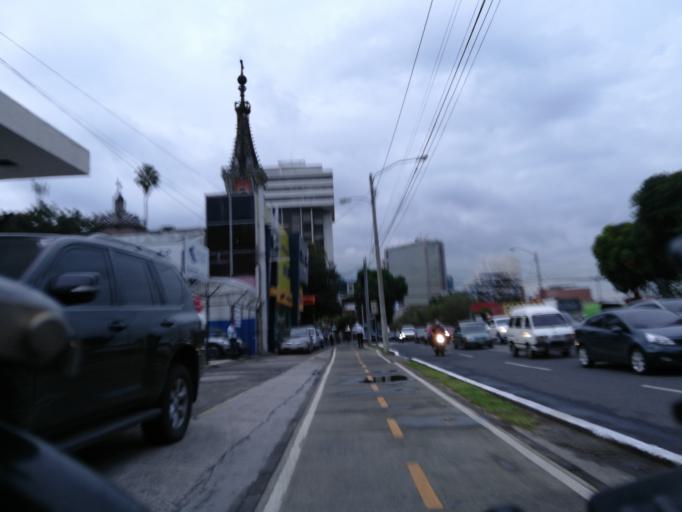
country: GT
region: Guatemala
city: Guatemala City
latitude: 14.6155
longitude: -90.5144
